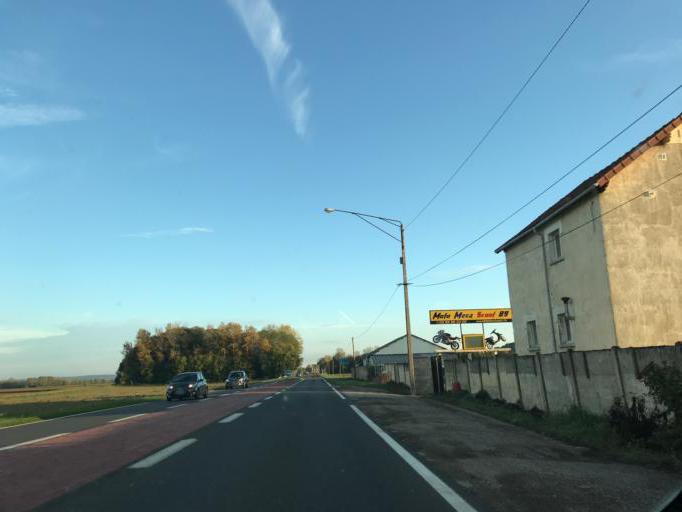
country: FR
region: Bourgogne
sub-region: Departement de l'Yonne
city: Pont-sur-Yonne
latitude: 48.2811
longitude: 3.2161
